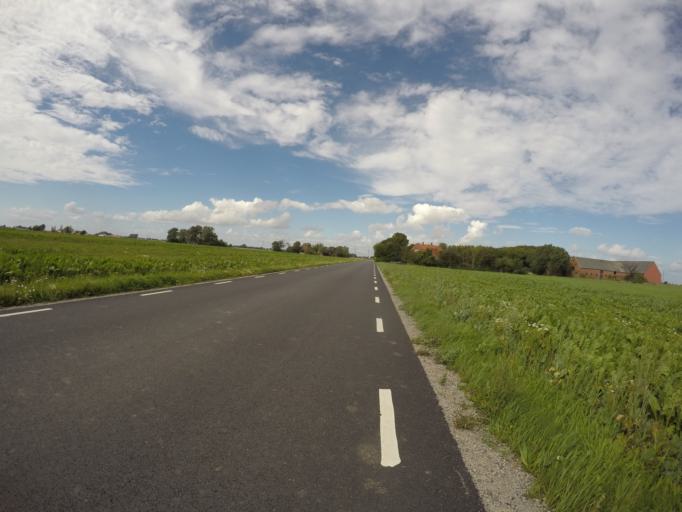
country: SE
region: Skane
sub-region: Ystads Kommun
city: Kopingebro
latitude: 55.4151
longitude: 14.1509
